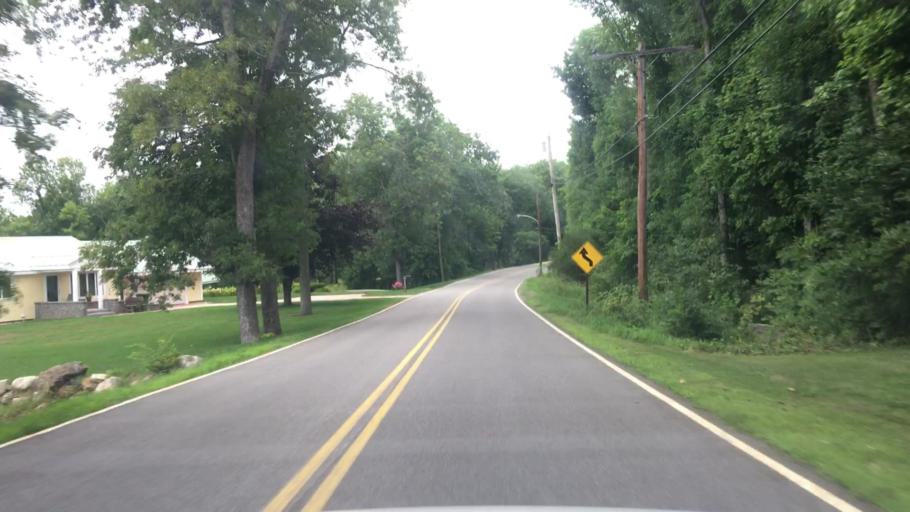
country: US
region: Maine
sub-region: York County
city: Dayton
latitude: 43.5337
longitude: -70.5158
